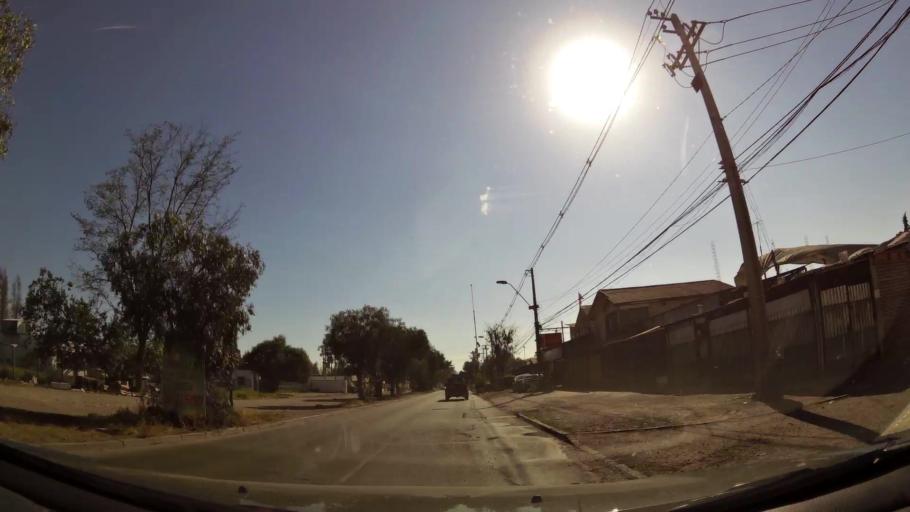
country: CL
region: Santiago Metropolitan
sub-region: Provincia de Santiago
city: La Pintana
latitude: -33.5869
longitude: -70.6482
